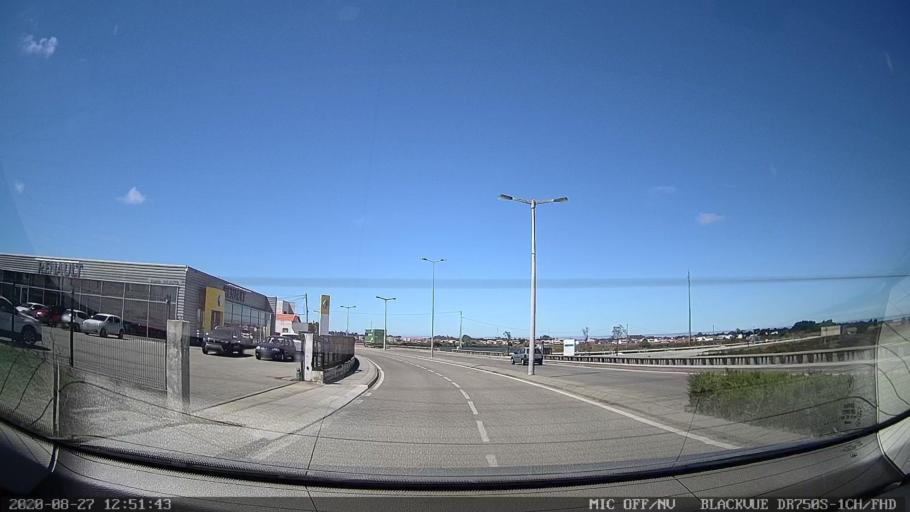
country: PT
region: Aveiro
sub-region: Ilhavo
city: Ilhavo
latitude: 40.6073
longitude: -8.6744
